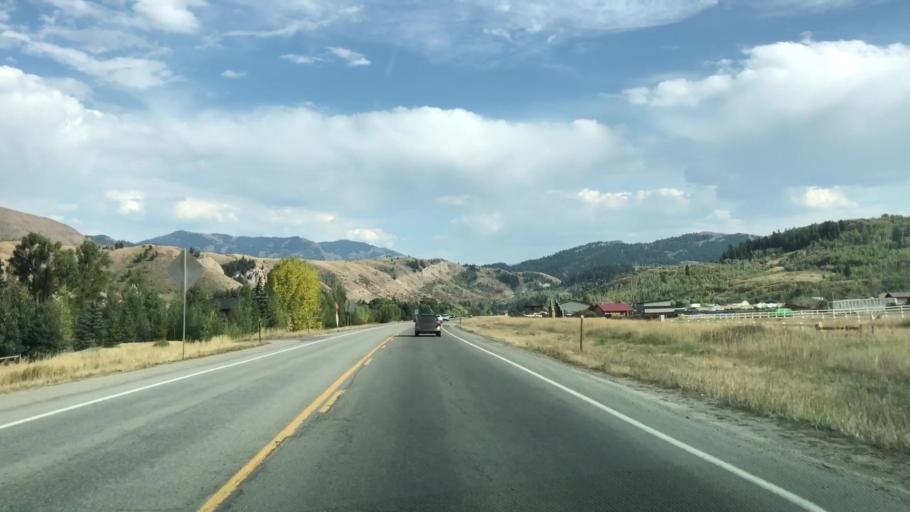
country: US
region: Wyoming
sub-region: Teton County
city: South Park
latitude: 43.3696
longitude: -110.7379
